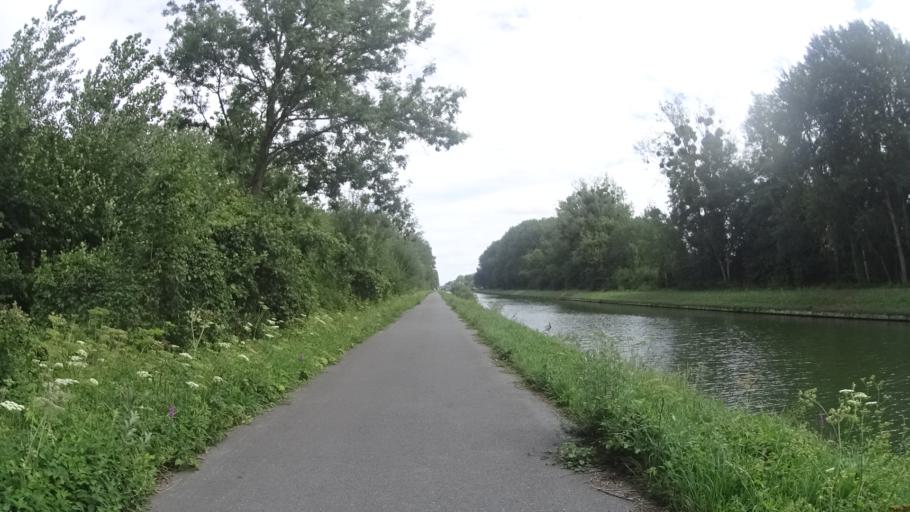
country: FR
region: Picardie
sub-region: Departement de l'Aisne
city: Blerancourt
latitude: 49.5773
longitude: 3.1007
